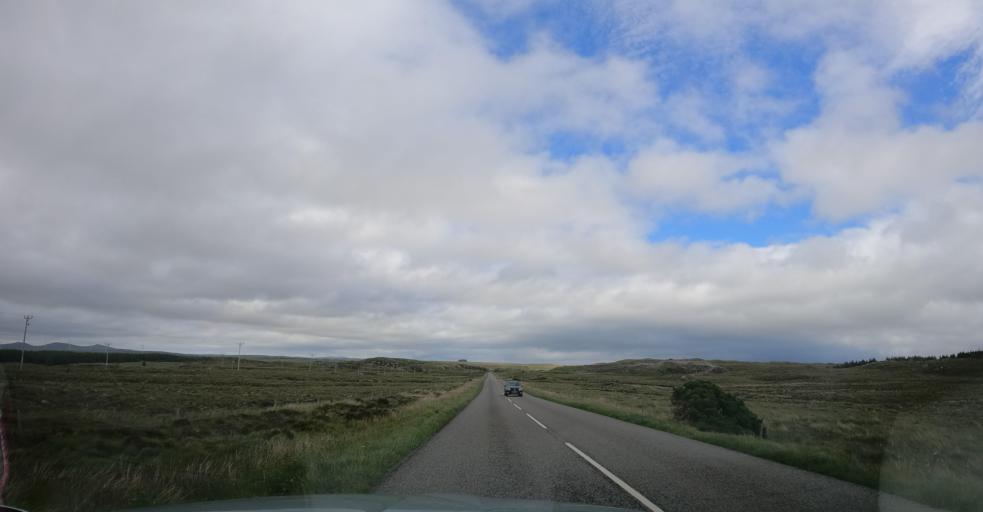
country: GB
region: Scotland
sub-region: Eilean Siar
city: Stornoway
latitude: 58.1690
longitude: -6.4805
